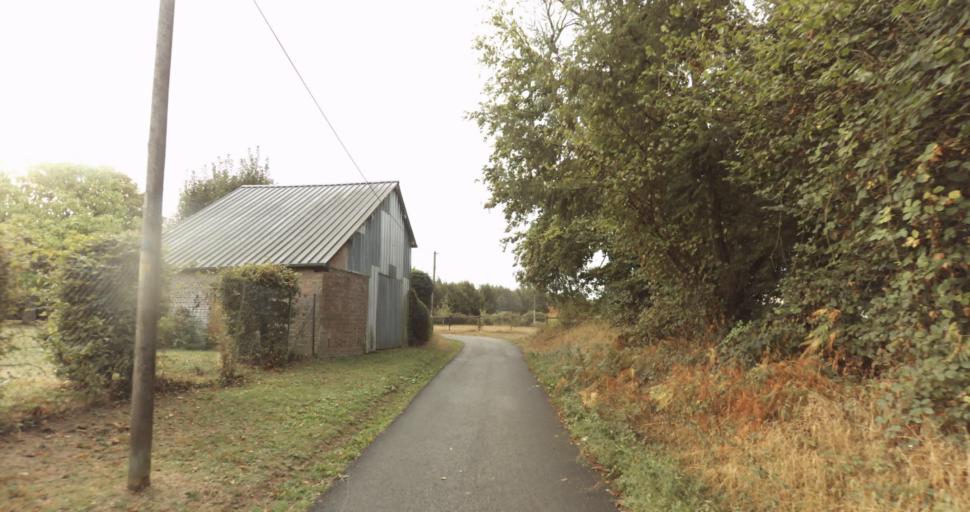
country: FR
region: Lower Normandy
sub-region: Departement de l'Orne
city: Vimoutiers
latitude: 48.9023
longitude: 0.2473
